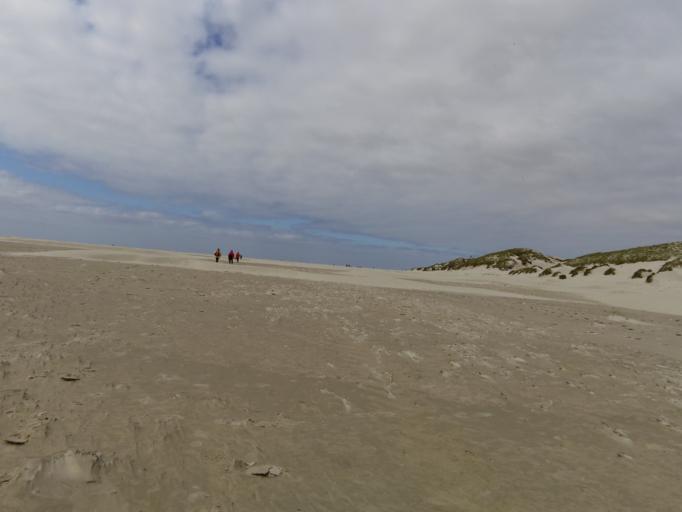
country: DE
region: Schleswig-Holstein
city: Nebel
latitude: 54.6219
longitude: 8.3585
